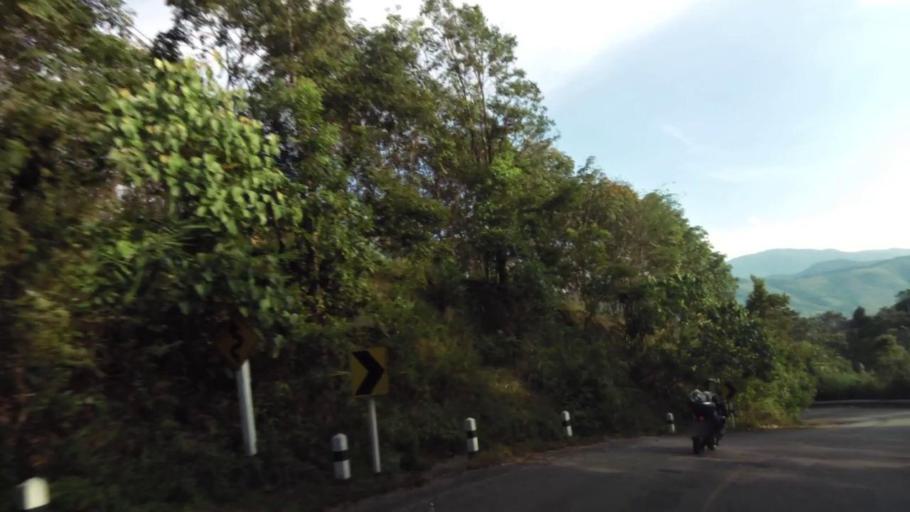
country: TH
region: Chiang Rai
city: Khun Tan
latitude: 19.8532
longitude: 100.3788
